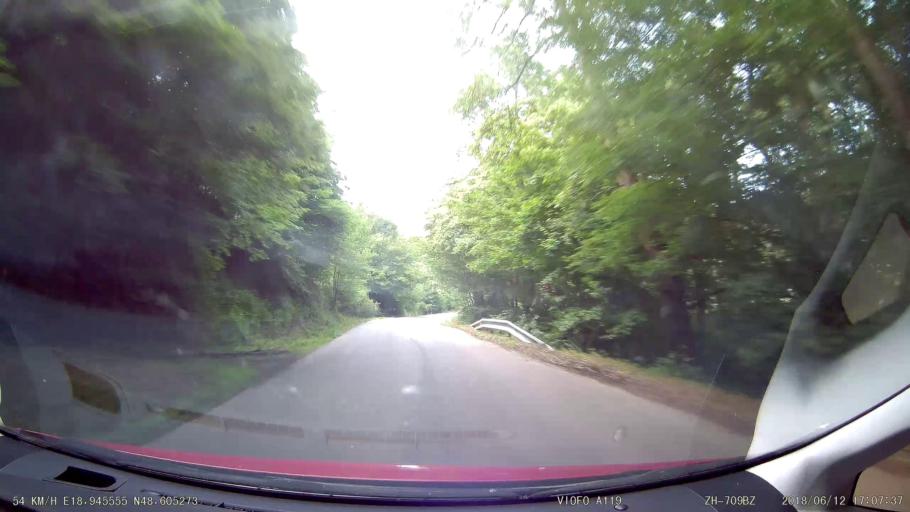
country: SK
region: Banskobystricky
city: Ziar nad Hronom
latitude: 48.6054
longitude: 18.9456
